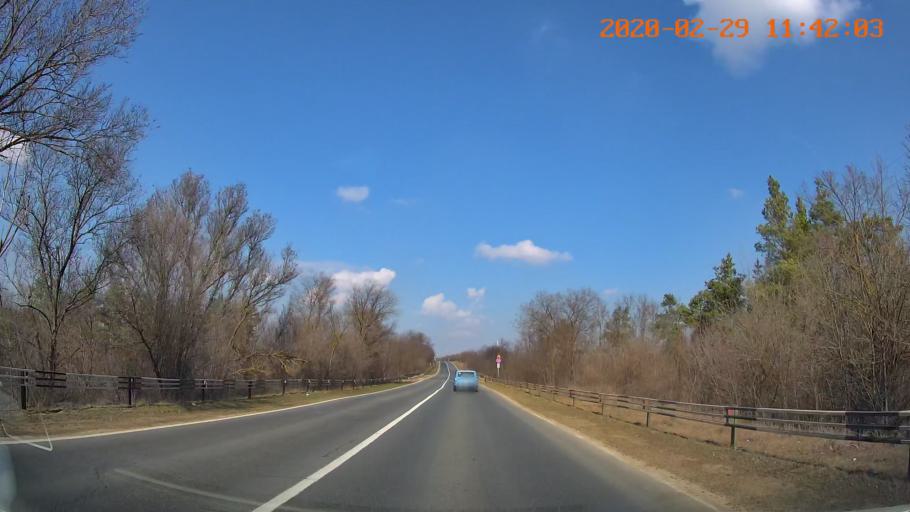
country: MD
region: Rezina
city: Saharna
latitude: 47.6791
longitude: 29.0145
